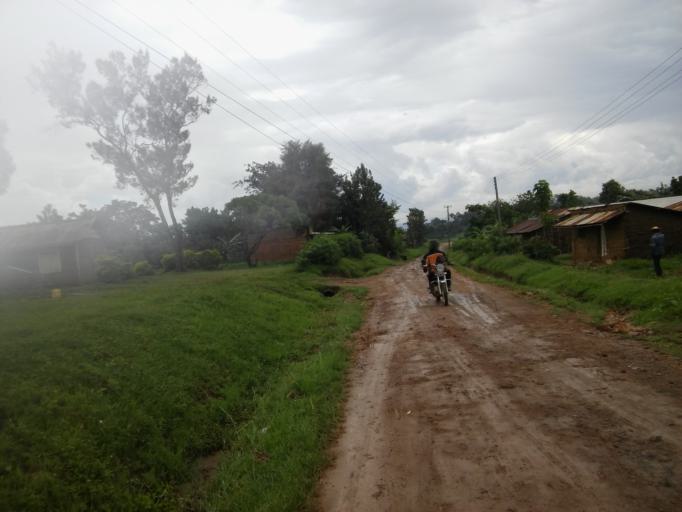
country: UG
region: Eastern Region
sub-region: Mbale District
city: Mbale
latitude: 1.0338
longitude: 34.1960
